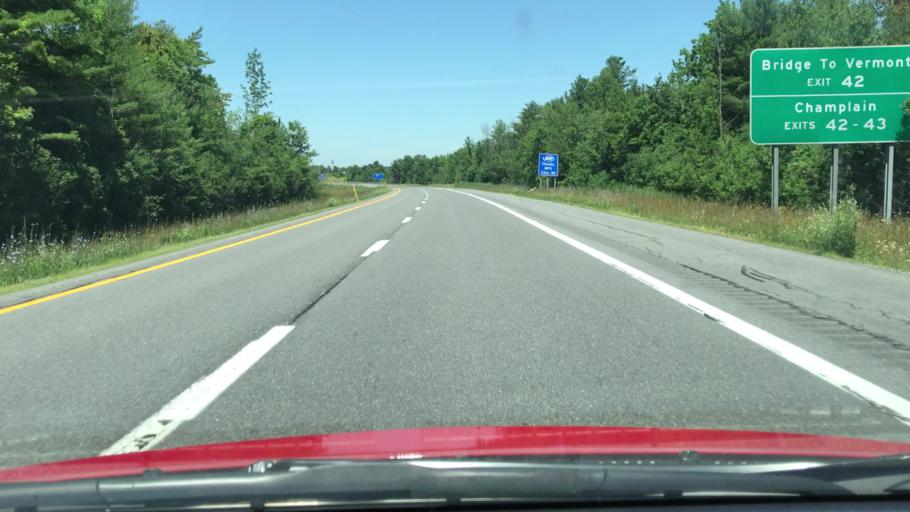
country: US
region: New York
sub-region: Clinton County
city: Champlain
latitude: 44.9664
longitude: -73.4498
